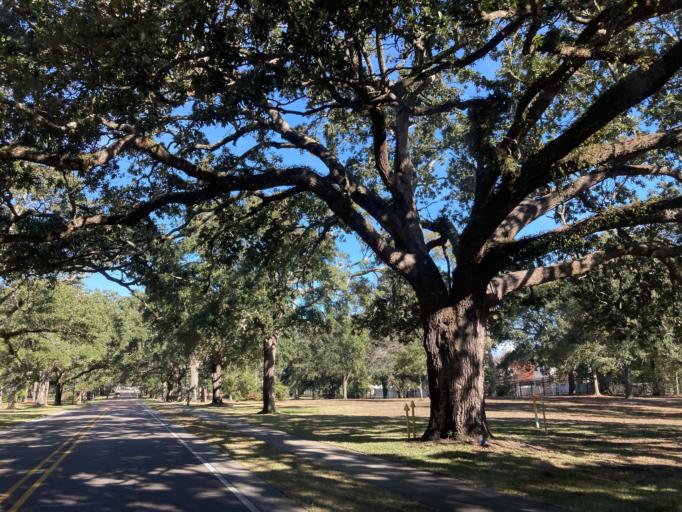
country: US
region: Mississippi
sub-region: Harrison County
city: D'Iberville
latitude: 30.4046
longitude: -88.9472
